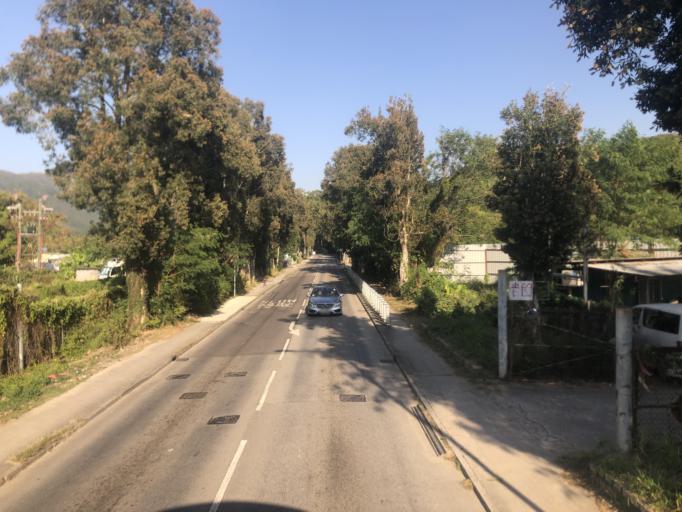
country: CN
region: Guangdong
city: Liantang
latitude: 22.5176
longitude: 114.1734
